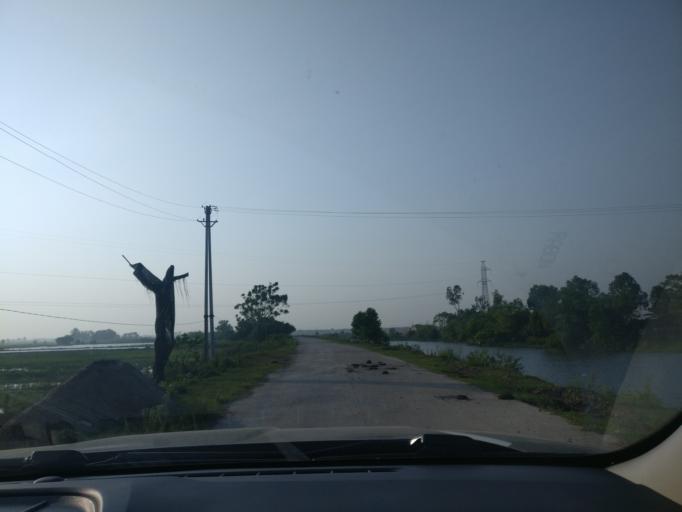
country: VN
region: Ninh Binh
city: Thanh Pho Ninh Binh
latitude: 20.2336
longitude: 105.9430
